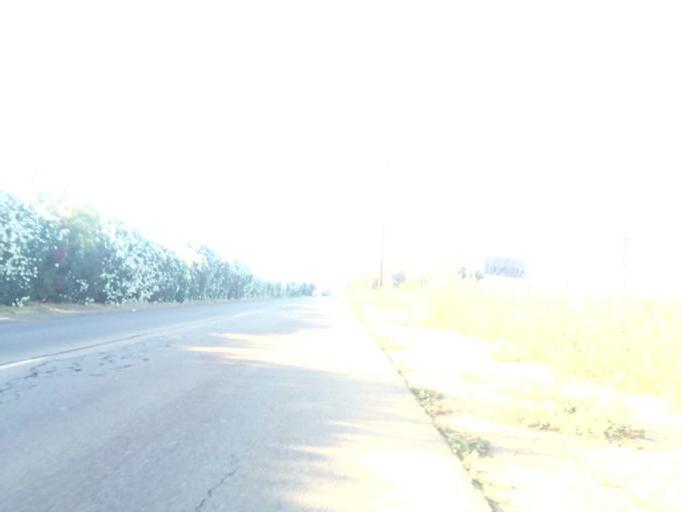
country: US
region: California
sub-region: Fresno County
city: Sunnyside
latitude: 36.7663
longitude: -119.6822
